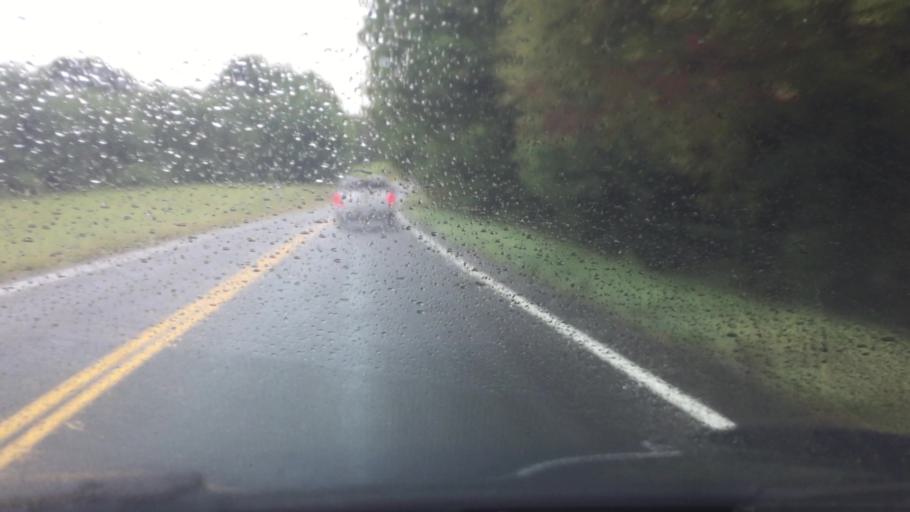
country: US
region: Virginia
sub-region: Bedford County
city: Forest
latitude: 37.3663
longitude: -79.3955
